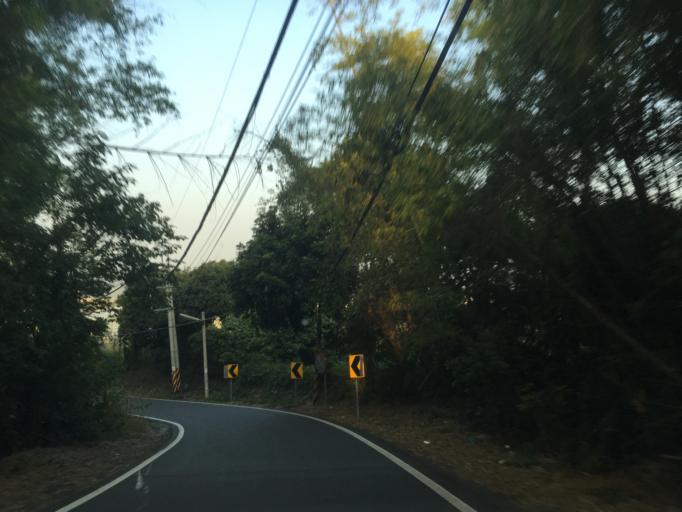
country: TW
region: Taiwan
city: Zhongxing New Village
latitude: 23.9472
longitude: 120.6589
